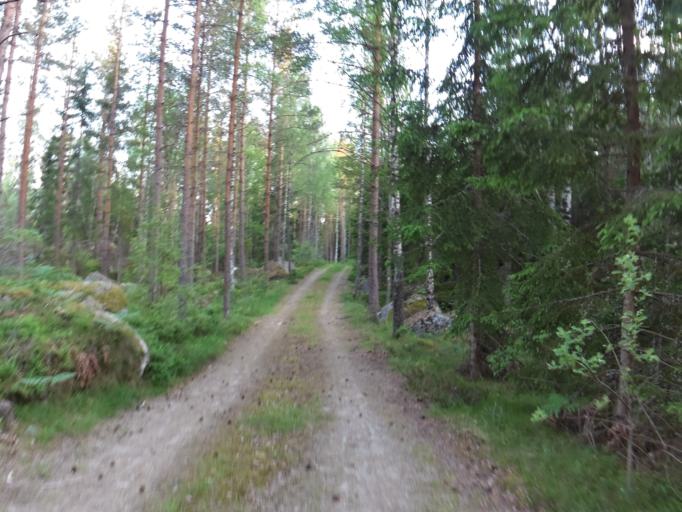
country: SE
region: Blekinge
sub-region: Olofstroms Kommun
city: Olofstroem
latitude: 56.4083
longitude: 14.5437
